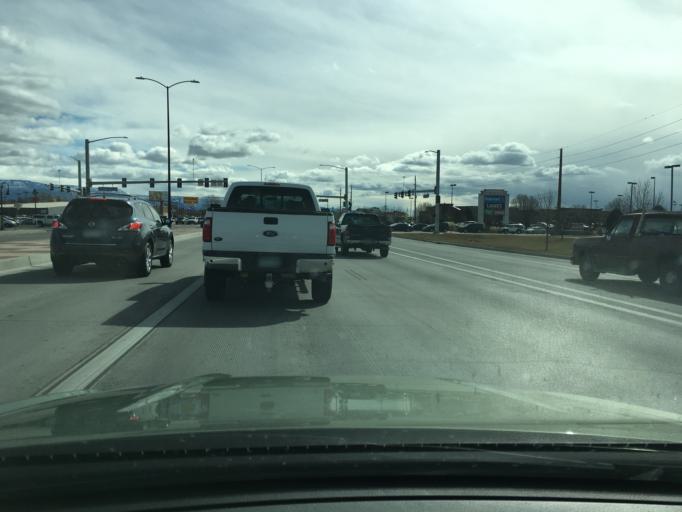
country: US
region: Colorado
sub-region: Mesa County
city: Grand Junction
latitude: 39.0810
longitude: -108.5845
